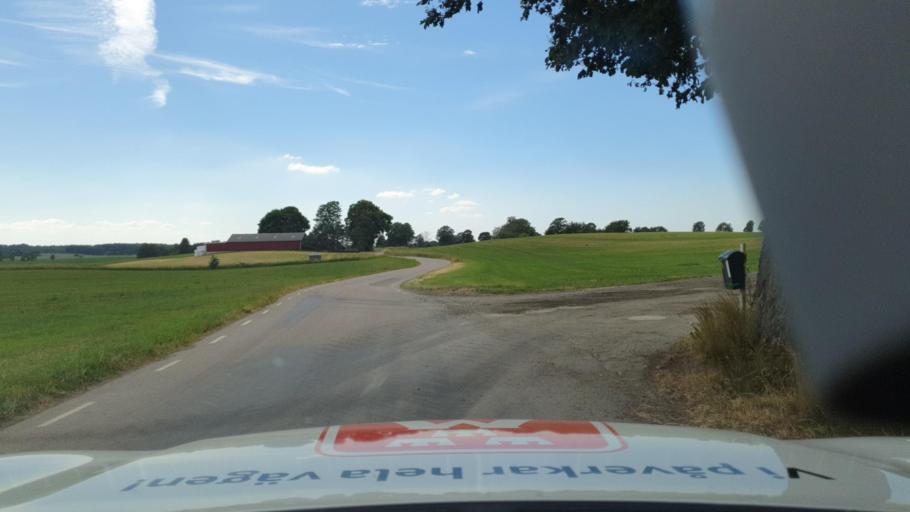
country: SE
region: Skane
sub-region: Tomelilla Kommun
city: Tomelilla
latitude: 55.6281
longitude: 13.8490
